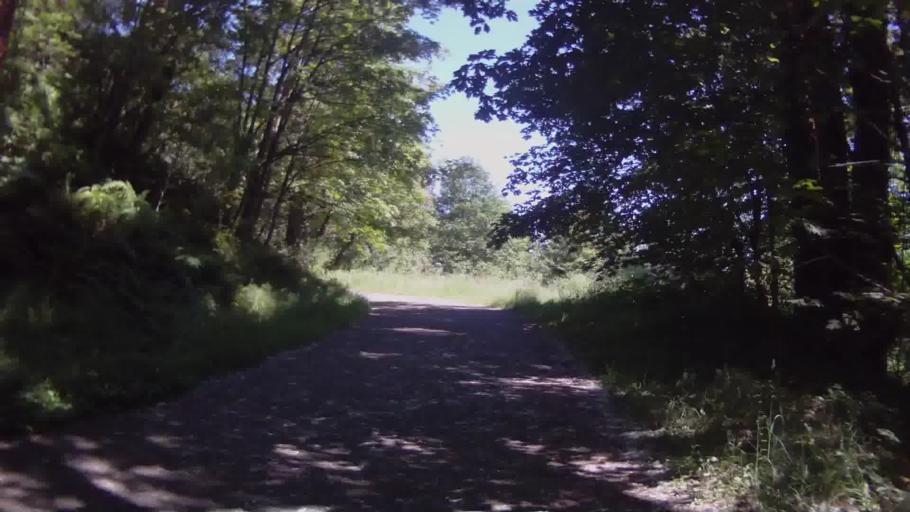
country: US
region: Oregon
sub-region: Washington County
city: West Haven-Sylvan
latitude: 45.5436
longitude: -122.7269
